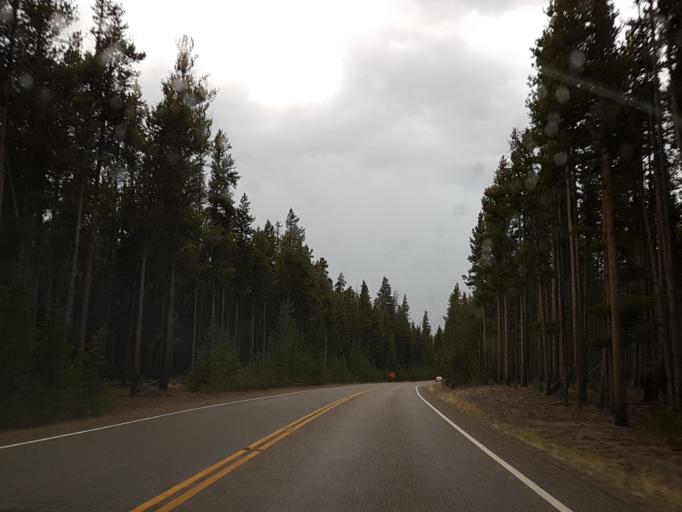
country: US
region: Montana
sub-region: Gallatin County
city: West Yellowstone
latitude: 44.4635
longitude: -110.5145
